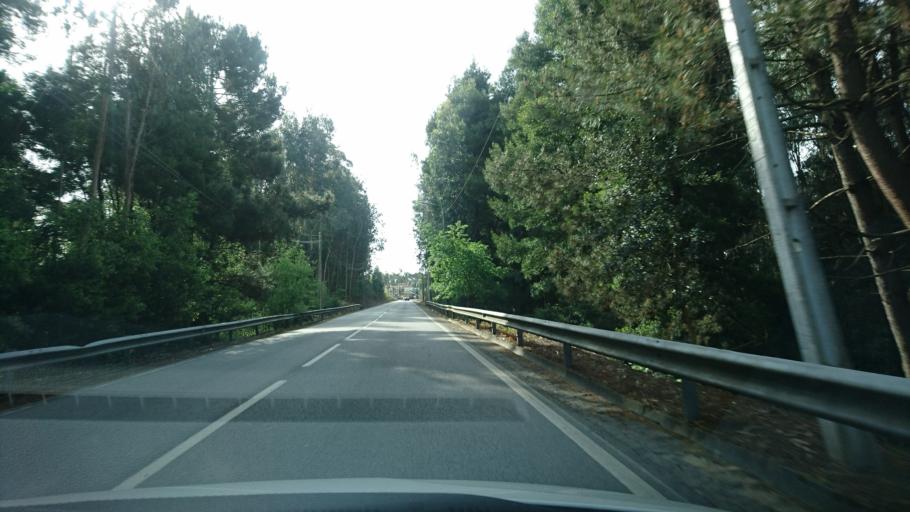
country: PT
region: Aveiro
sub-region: Oliveira de Azemeis
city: Vila Cha
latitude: 40.8622
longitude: -8.4750
